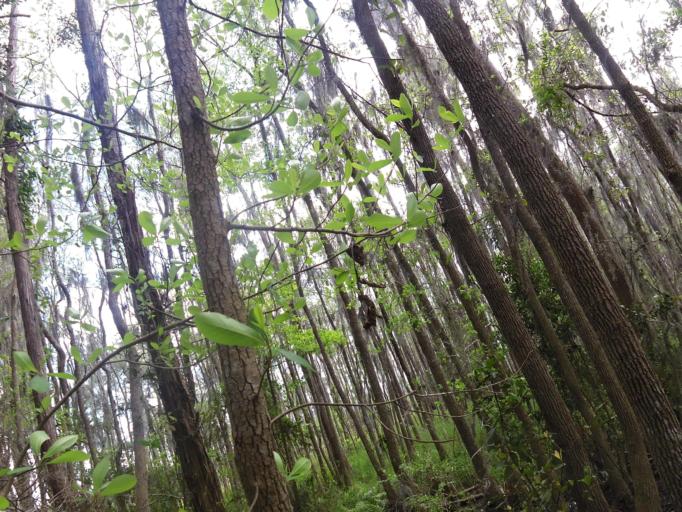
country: US
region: Georgia
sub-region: Charlton County
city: Folkston
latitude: 30.7126
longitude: -82.1636
